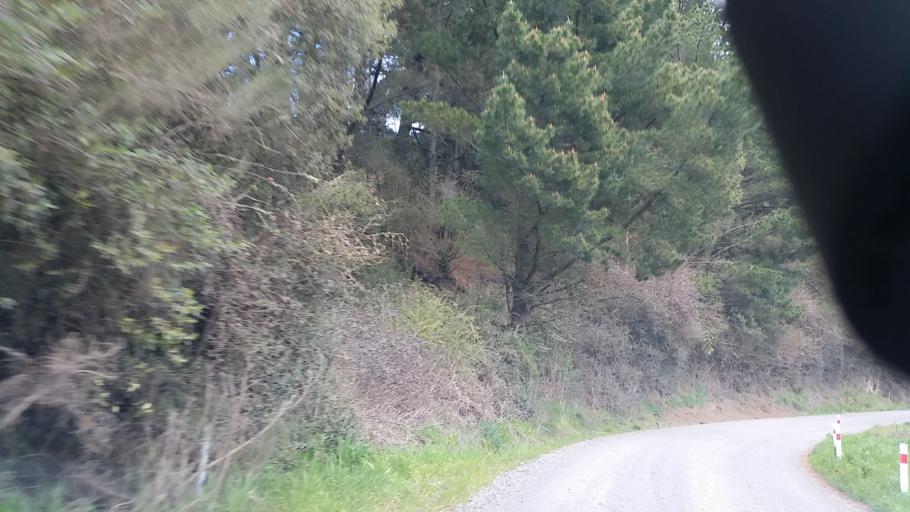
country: NZ
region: Bay of Plenty
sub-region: Rotorua District
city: Rotorua
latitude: -38.3868
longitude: 176.1718
